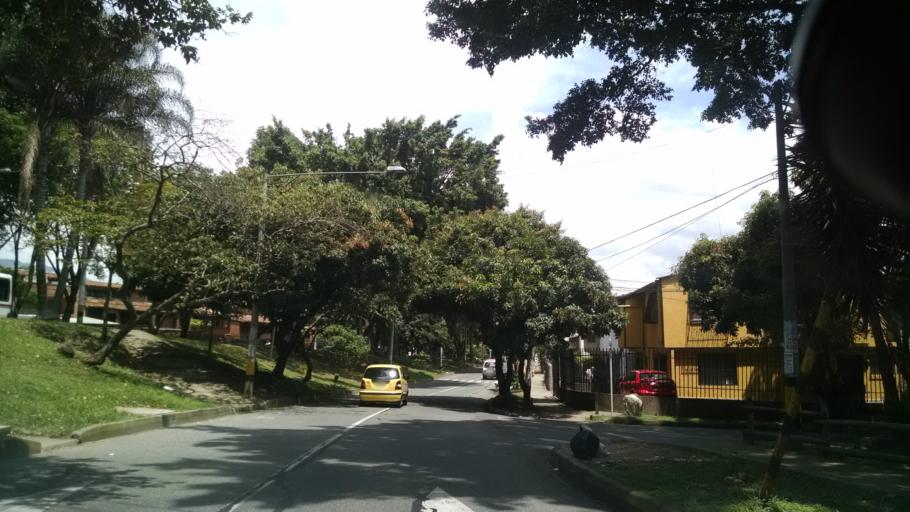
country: CO
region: Antioquia
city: Itagui
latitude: 6.2077
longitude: -75.5890
